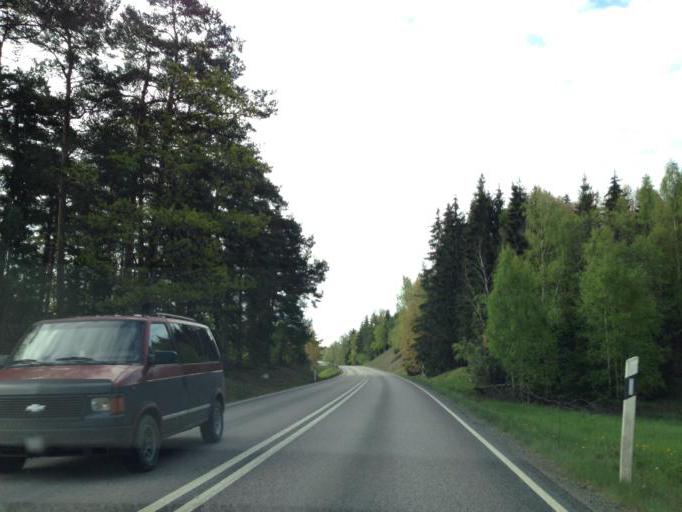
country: SE
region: Soedermanland
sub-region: Flens Kommun
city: Malmkoping
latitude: 59.0430
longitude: 16.8364
